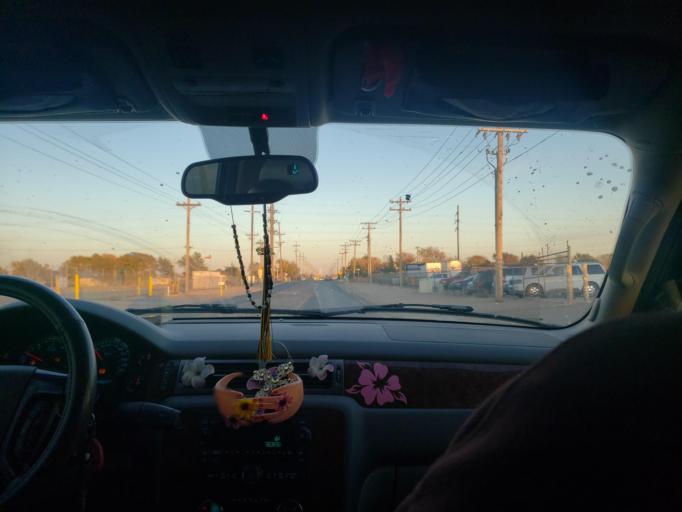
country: US
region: Kansas
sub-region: Finney County
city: Garden City
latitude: 37.9895
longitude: -100.8943
